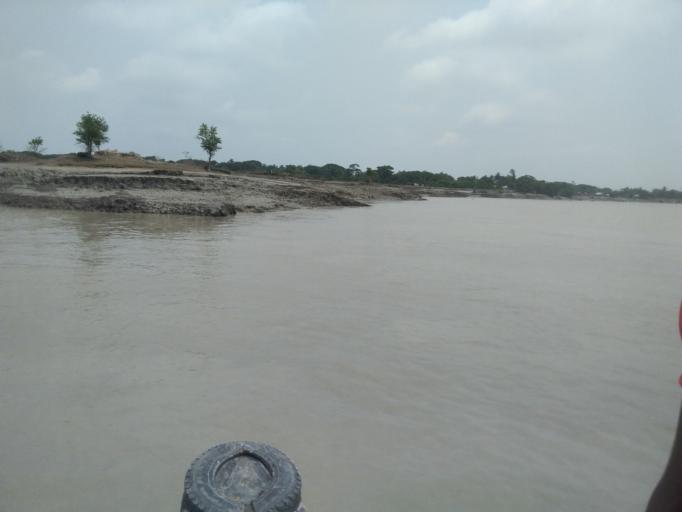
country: BD
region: Khulna
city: Phultala
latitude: 22.6453
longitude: 89.4110
